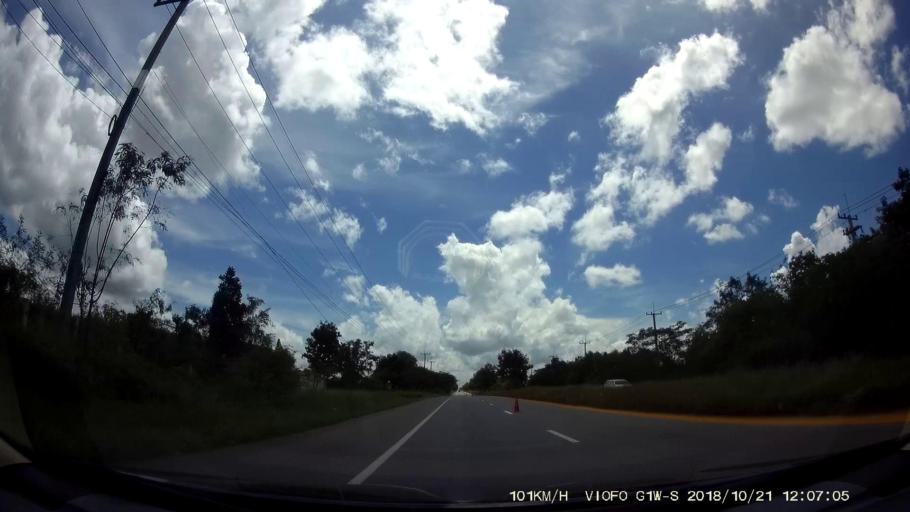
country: TH
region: Chaiyaphum
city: Chatturat
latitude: 15.4531
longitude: 101.8276
